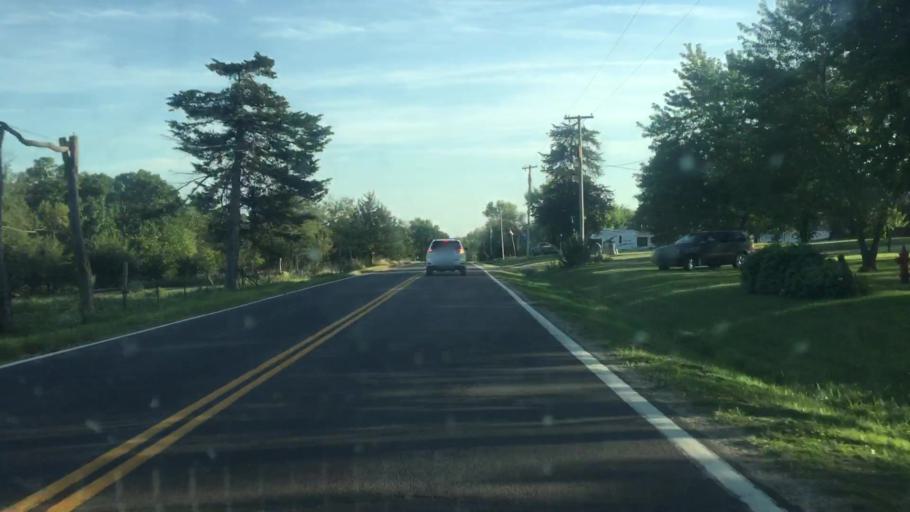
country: US
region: Kansas
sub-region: Brown County
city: Horton
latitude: 39.5559
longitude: -95.5246
